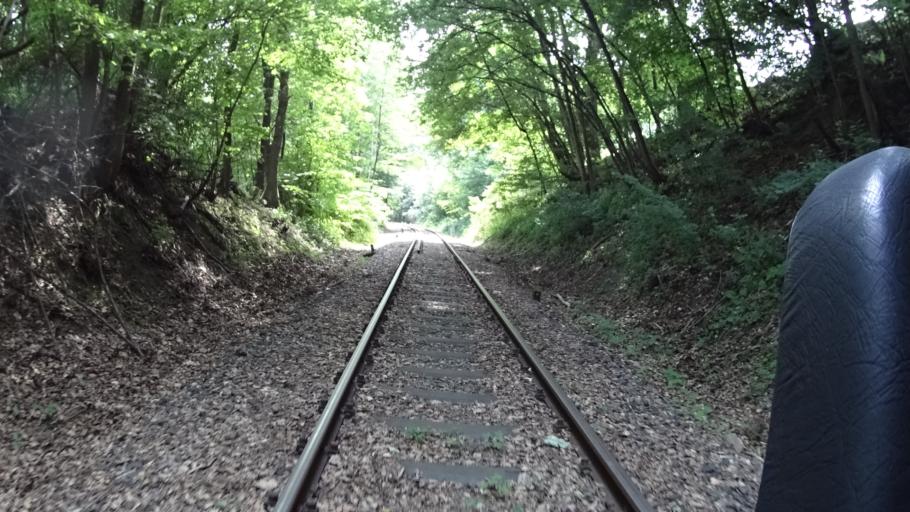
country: DE
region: Hesse
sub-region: Regierungsbezirk Darmstadt
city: Wald-Michelbach
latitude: 49.5629
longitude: 8.7967
